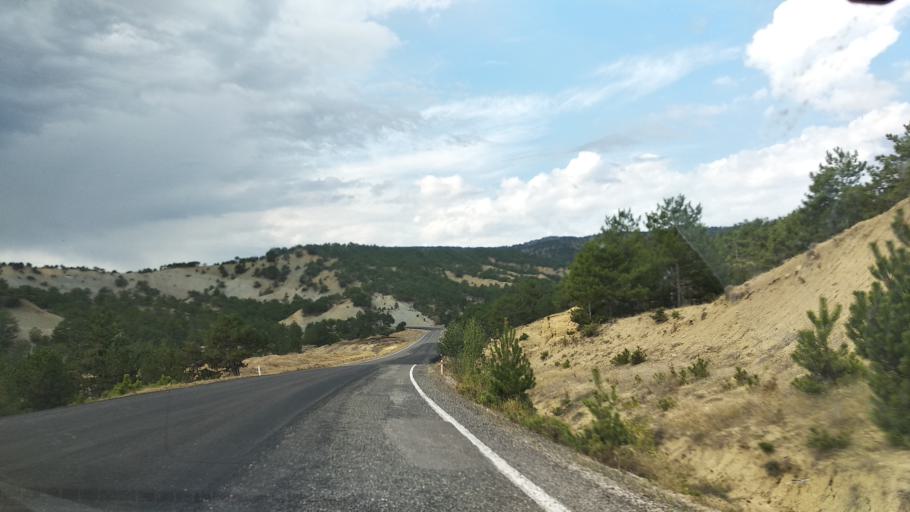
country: TR
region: Bolu
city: Seben
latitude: 40.3587
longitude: 31.4868
